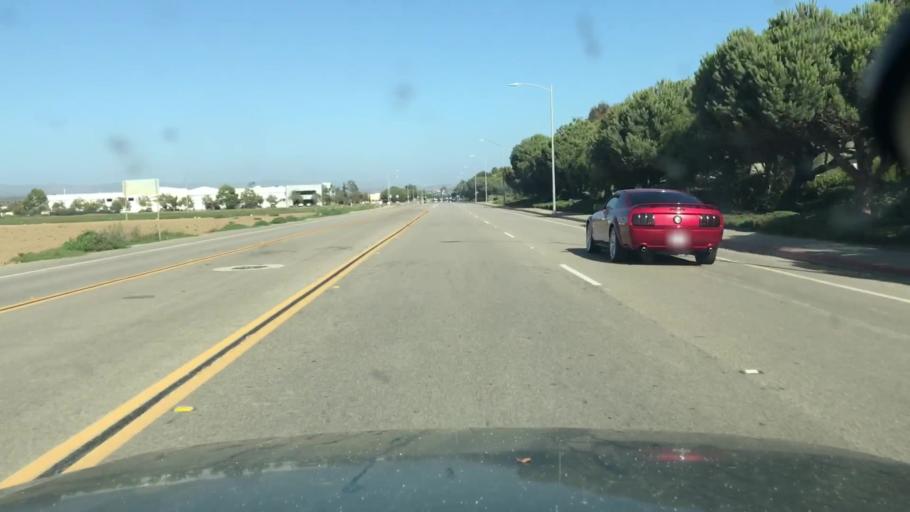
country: US
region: California
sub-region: Santa Barbara County
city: Lompoc
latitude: 34.6610
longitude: -120.4731
